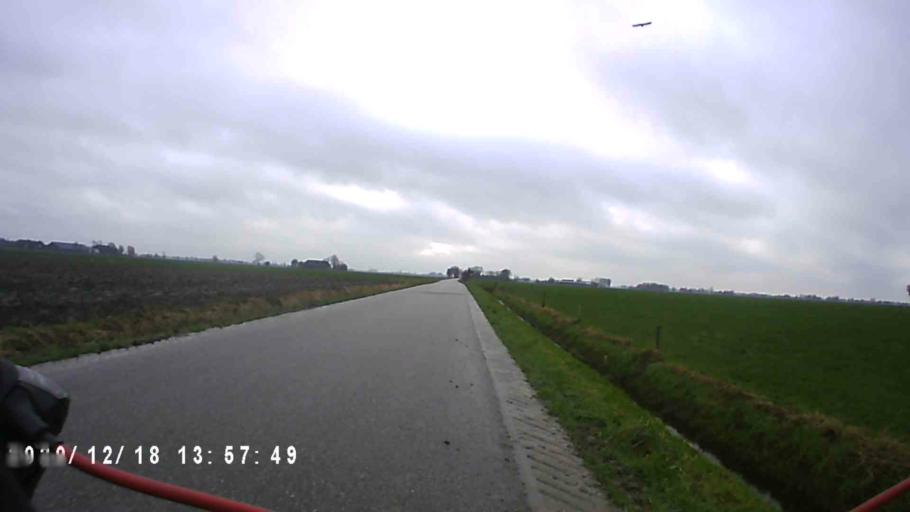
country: NL
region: Groningen
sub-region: Gemeente Bedum
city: Bedum
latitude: 53.2999
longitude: 6.6265
